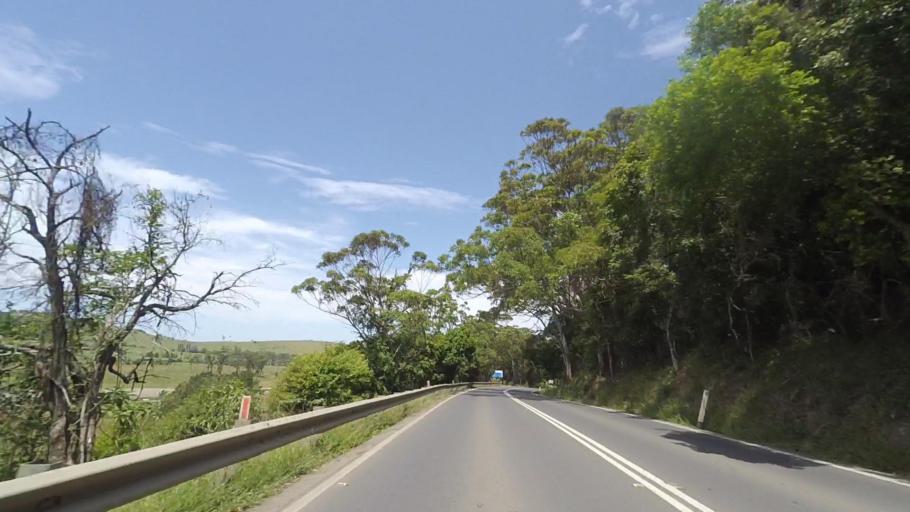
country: AU
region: New South Wales
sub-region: Shoalhaven Shire
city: Berry
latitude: -34.7519
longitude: 150.7499
